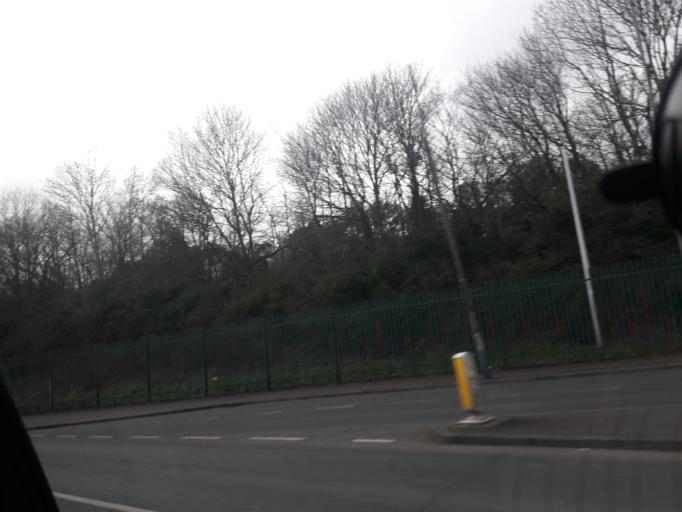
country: GB
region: Northern Ireland
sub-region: City of Belfast
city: Belfast
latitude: 54.6248
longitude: -5.9484
